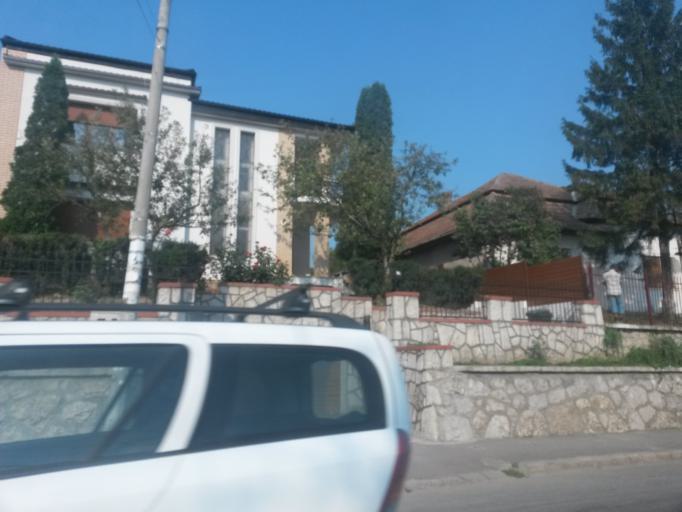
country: RO
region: Cluj
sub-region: Comuna Sandulesti
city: Copaceni
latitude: 46.5843
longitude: 23.7624
